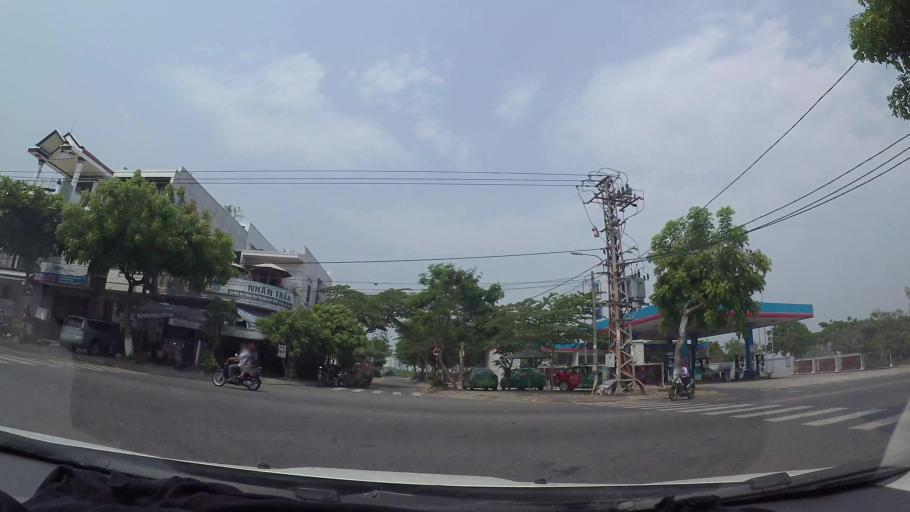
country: VN
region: Da Nang
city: Cam Le
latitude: 16.0041
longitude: 108.2074
